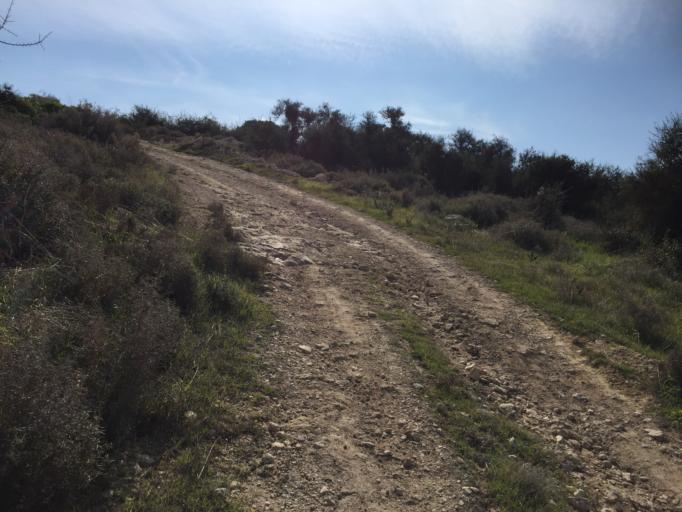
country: CY
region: Larnaka
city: Agios Tychon
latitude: 34.7435
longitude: 33.1182
